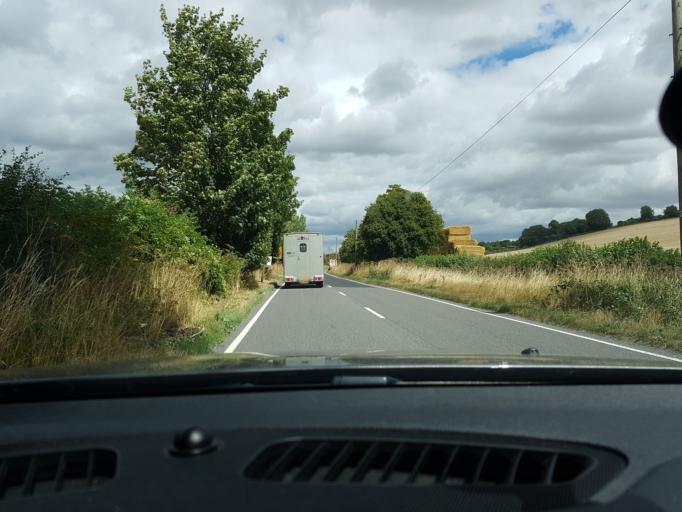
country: GB
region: England
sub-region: West Berkshire
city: Welford
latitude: 51.4845
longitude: -1.4379
